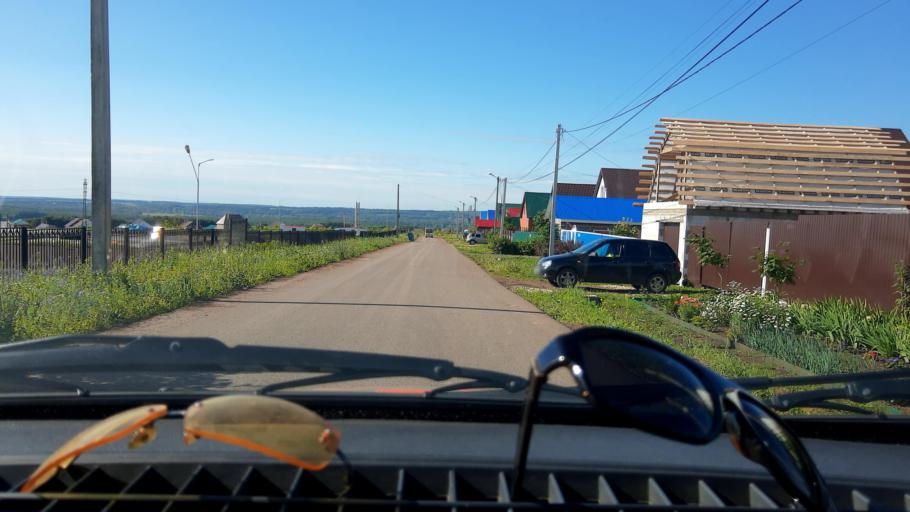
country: RU
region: Bashkortostan
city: Avdon
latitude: 54.6531
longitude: 55.7376
